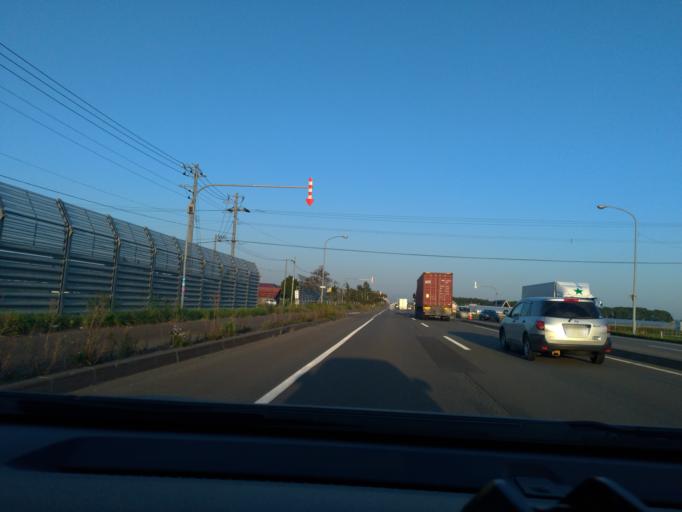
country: JP
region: Hokkaido
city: Tobetsu
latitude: 43.1777
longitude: 141.4420
